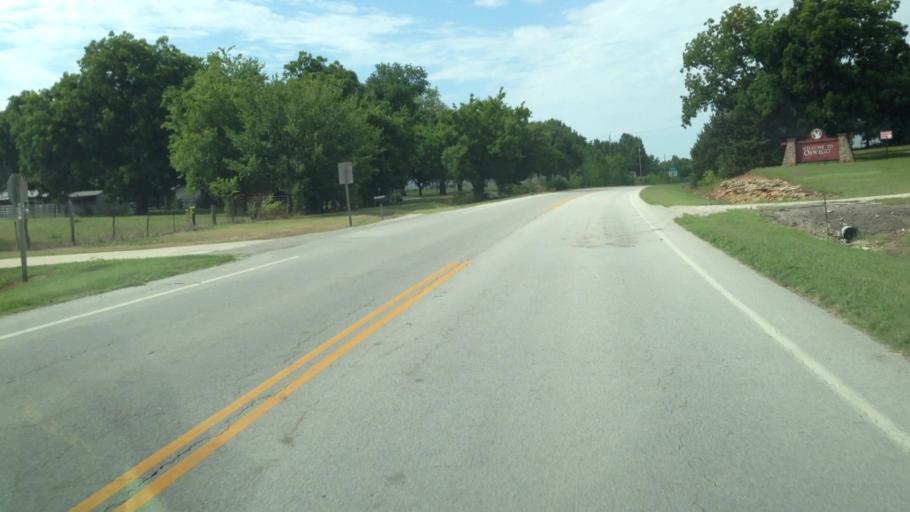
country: US
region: Kansas
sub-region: Labette County
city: Oswego
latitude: 37.1556
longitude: -95.1084
